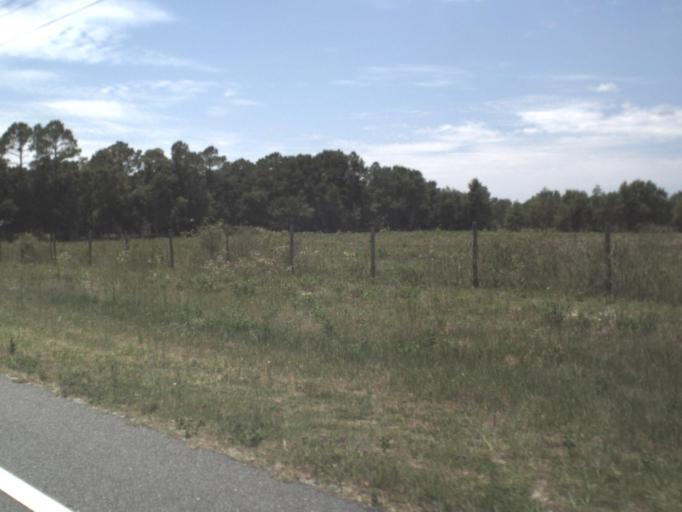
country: US
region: Florida
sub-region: Dixie County
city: Cross City
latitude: 29.7585
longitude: -82.9826
